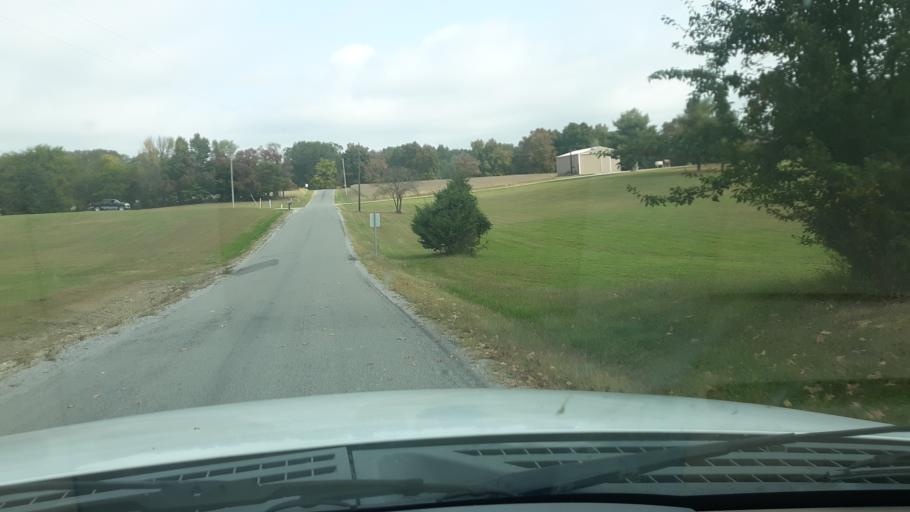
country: US
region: Illinois
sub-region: Saline County
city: Eldorado
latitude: 37.8340
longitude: -88.4849
